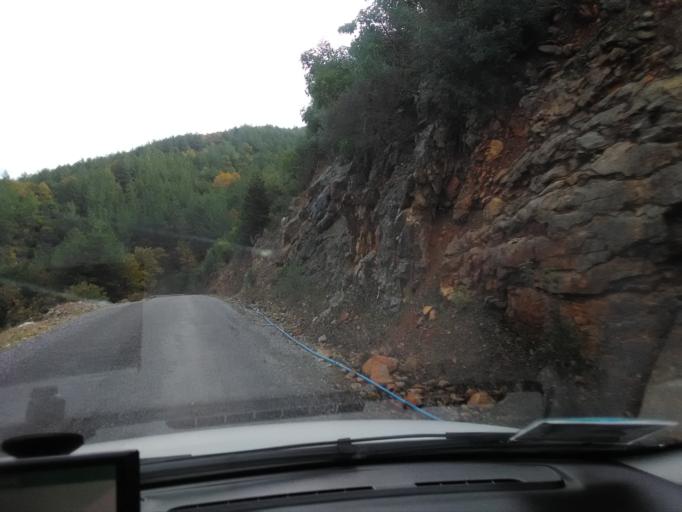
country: TR
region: Antalya
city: Gazipasa
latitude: 36.2455
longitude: 32.4358
